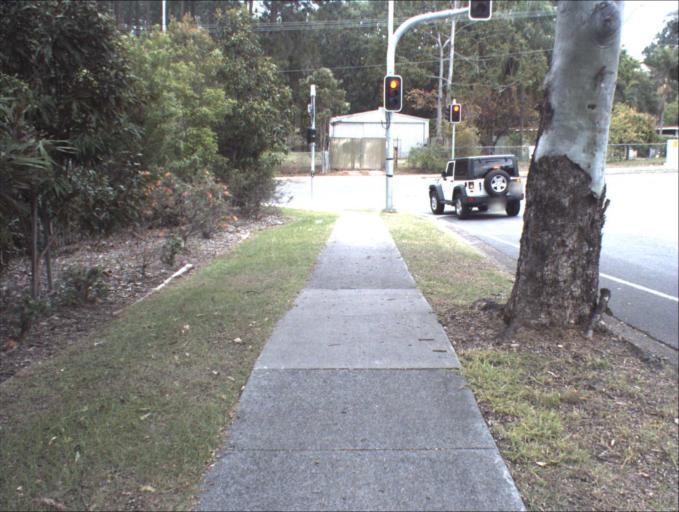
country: AU
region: Queensland
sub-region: Logan
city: Park Ridge South
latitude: -27.6867
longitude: 153.0350
